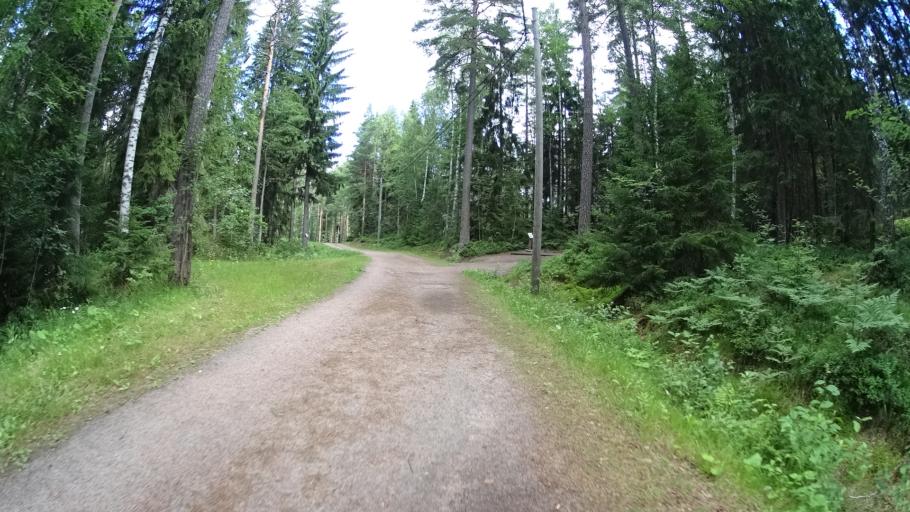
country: FI
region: Uusimaa
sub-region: Helsinki
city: Espoo
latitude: 60.2370
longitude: 24.6718
